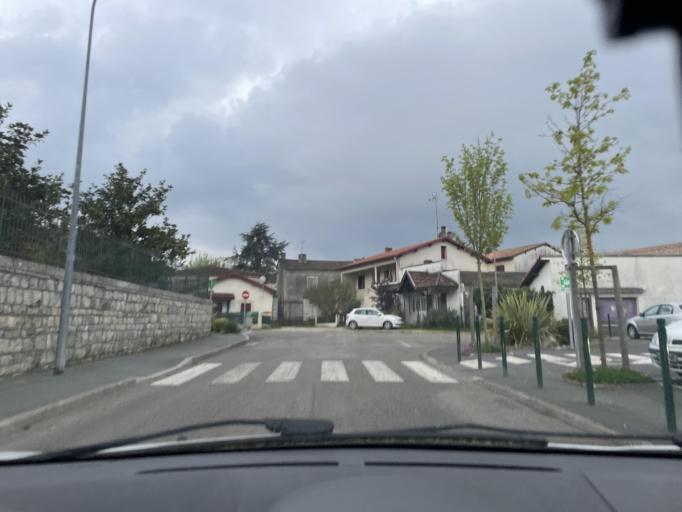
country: FR
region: Aquitaine
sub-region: Departement du Lot-et-Garonne
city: Casteljaloux
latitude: 44.3162
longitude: 0.0880
